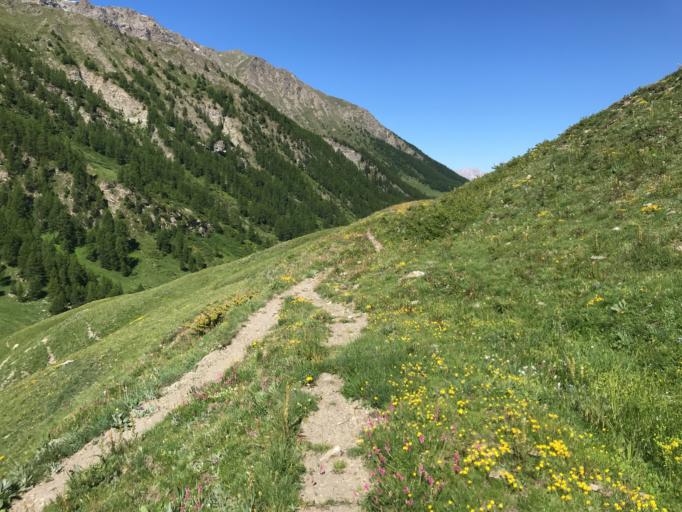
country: IT
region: Piedmont
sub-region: Provincia di Cuneo
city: Pontechianale
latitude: 44.7077
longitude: 6.9318
